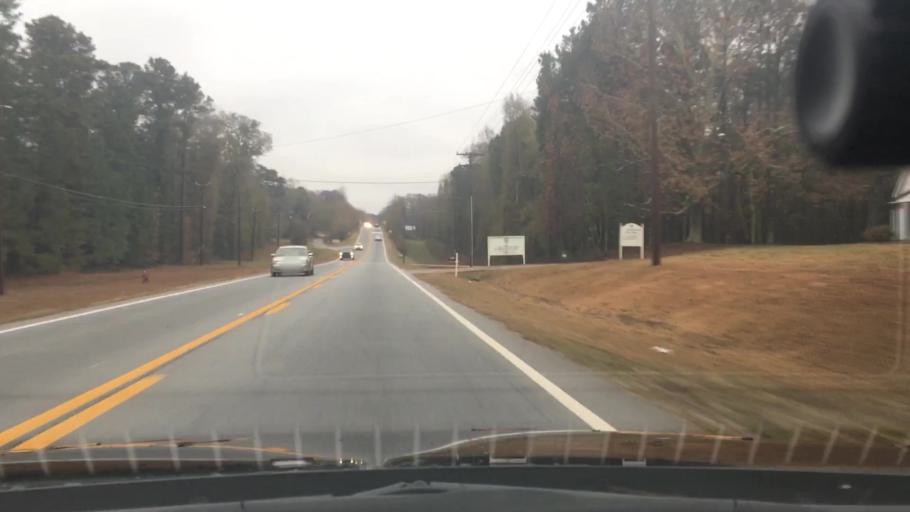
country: US
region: Georgia
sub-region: Fayette County
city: Peachtree City
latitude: 33.3349
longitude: -84.6471
